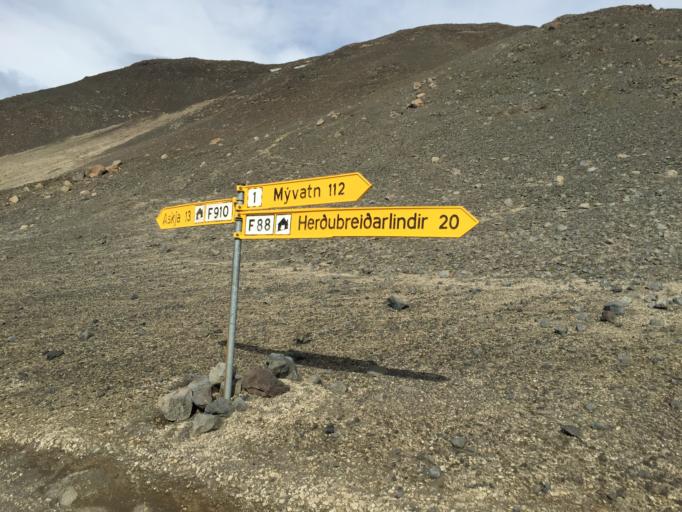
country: IS
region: Northeast
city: Laugar
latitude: 65.0722
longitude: -16.3800
